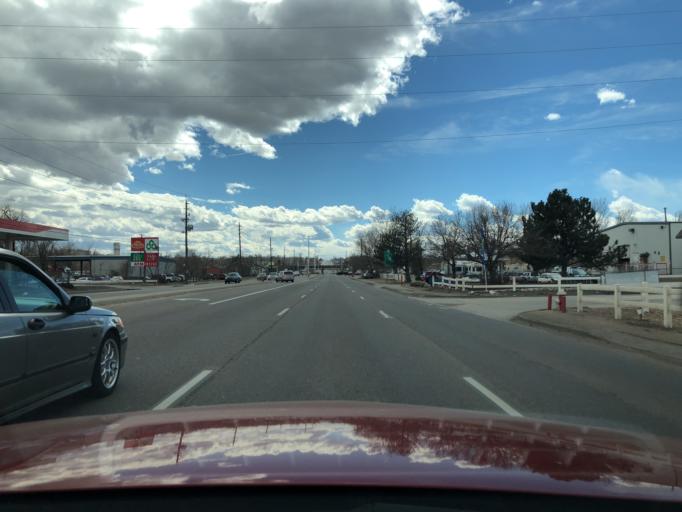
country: US
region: Colorado
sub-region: Adams County
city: Berkley
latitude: 39.8084
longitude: -105.0254
